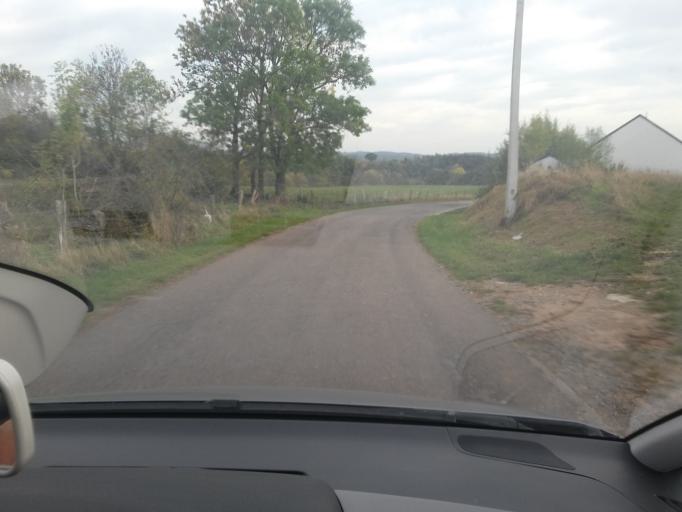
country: BE
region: Wallonia
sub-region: Province du Luxembourg
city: Attert
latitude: 49.7604
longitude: 5.7645
